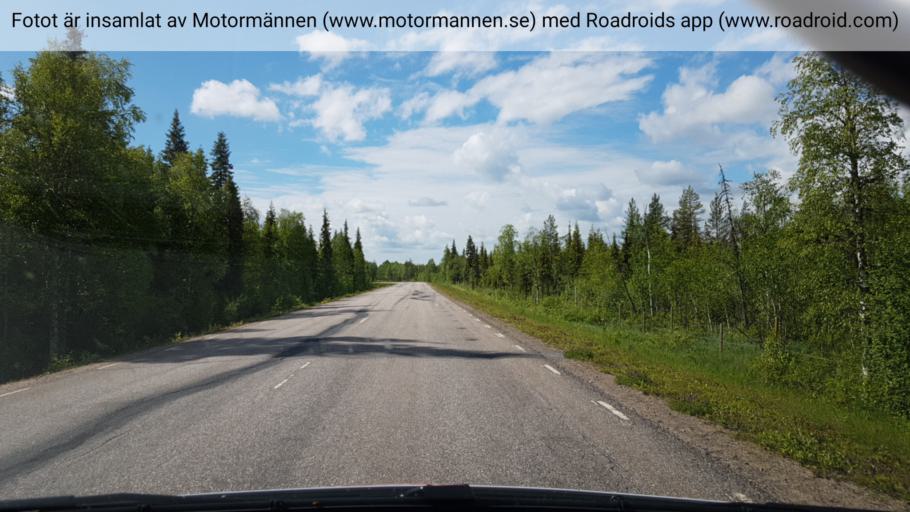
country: FI
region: Lapland
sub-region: Torniolaakso
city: Pello
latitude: 66.7665
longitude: 23.8704
